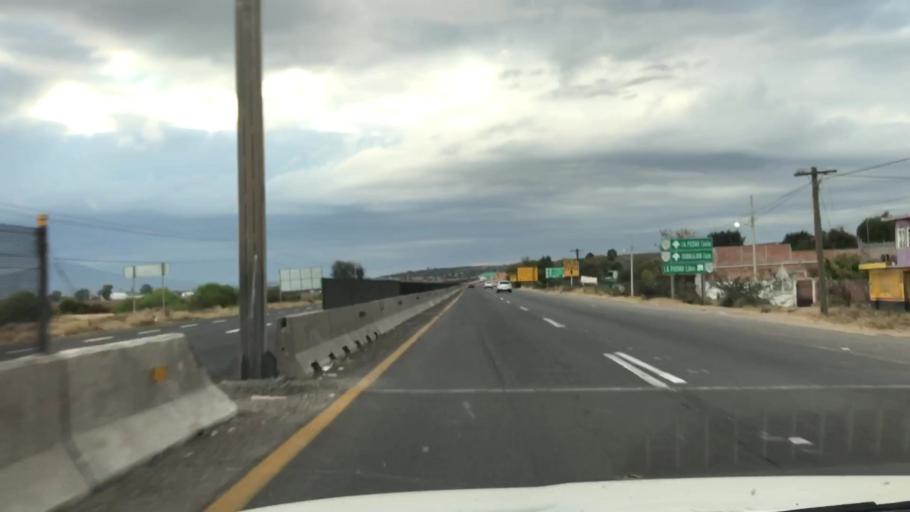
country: MX
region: Guanajuato
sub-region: Penjamo
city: Estacion la Piedad
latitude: 20.3883
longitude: -101.9437
